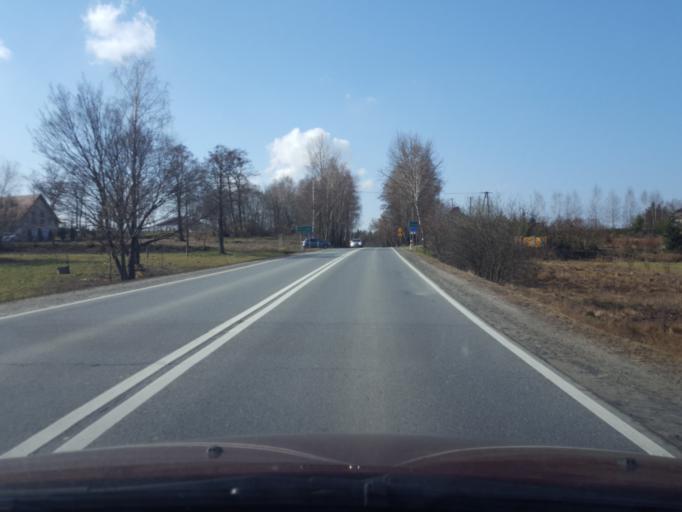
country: PL
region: Lesser Poland Voivodeship
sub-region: Powiat brzeski
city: Gnojnik
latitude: 49.8694
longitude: 20.6171
